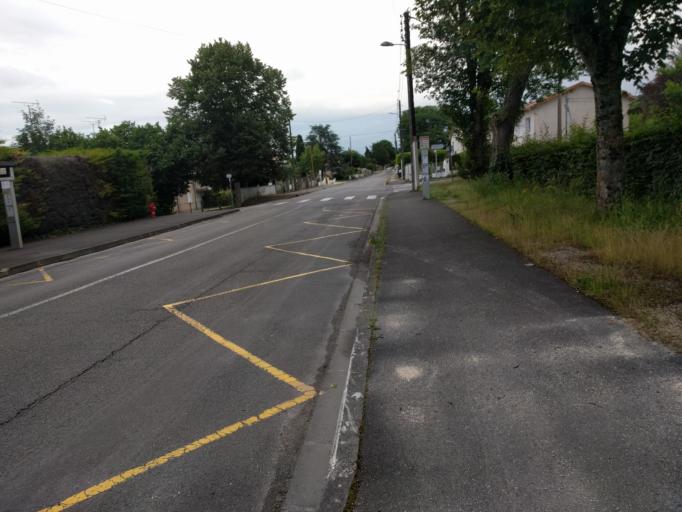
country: FR
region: Poitou-Charentes
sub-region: Departement de la Charente
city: Angouleme
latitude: 45.6356
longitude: 0.1581
